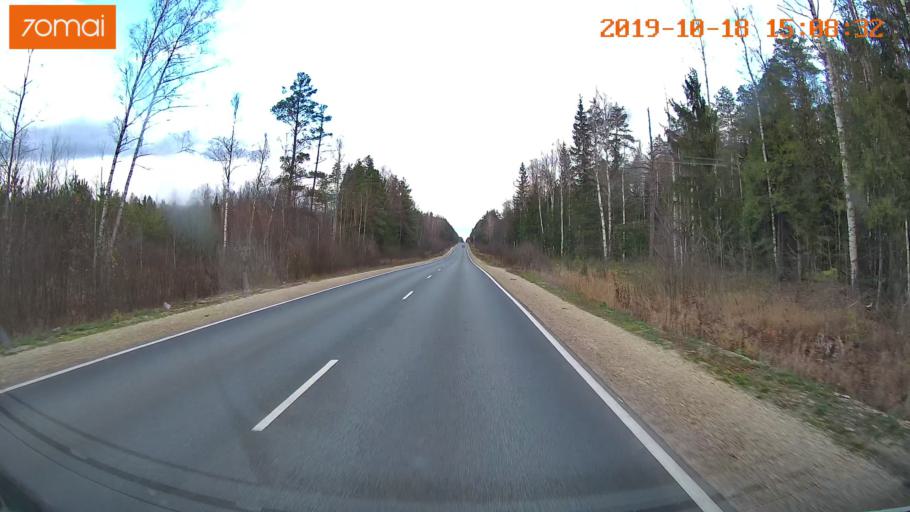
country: RU
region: Vladimir
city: Gus'-Khrustal'nyy
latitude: 55.5537
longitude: 40.6115
